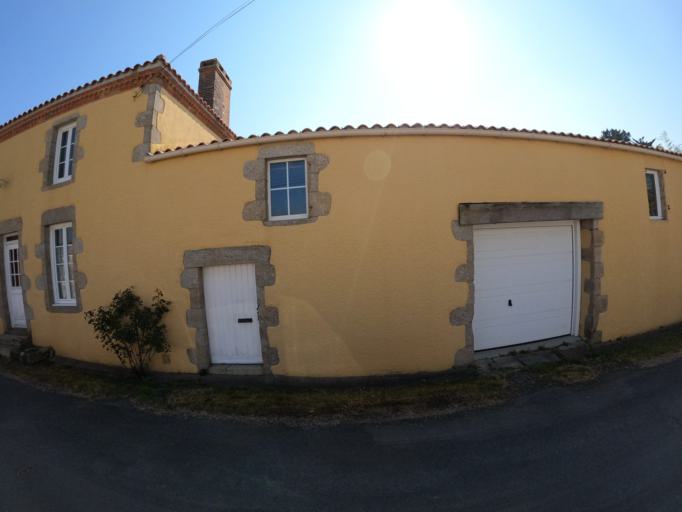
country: FR
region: Pays de la Loire
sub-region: Departement de la Loire-Atlantique
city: Aigrefeuille-sur-Maine
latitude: 47.0790
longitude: -1.4207
